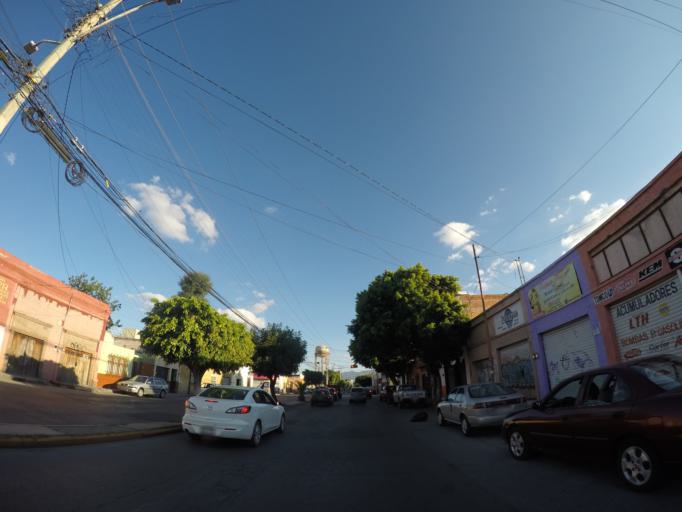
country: MX
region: San Luis Potosi
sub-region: San Luis Potosi
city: San Luis Potosi
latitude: 22.1650
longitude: -100.9805
